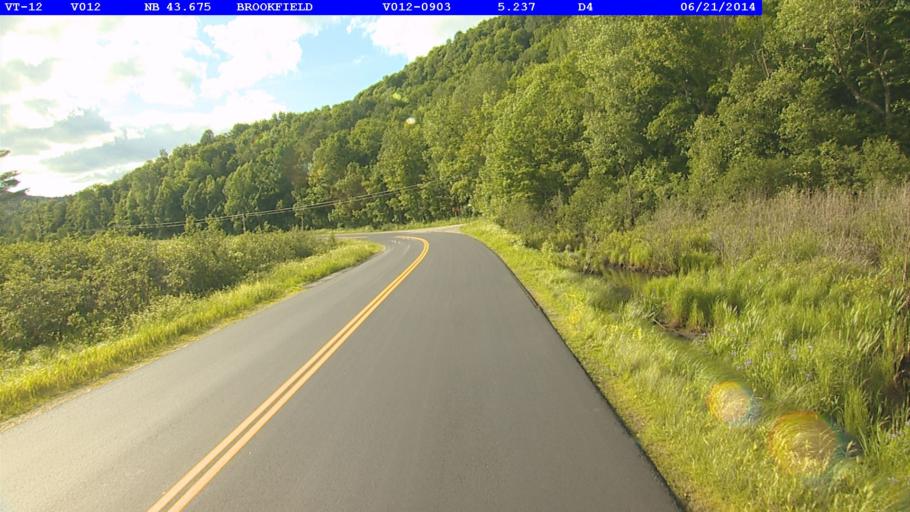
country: US
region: Vermont
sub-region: Washington County
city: Northfield
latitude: 44.0747
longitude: -72.6378
